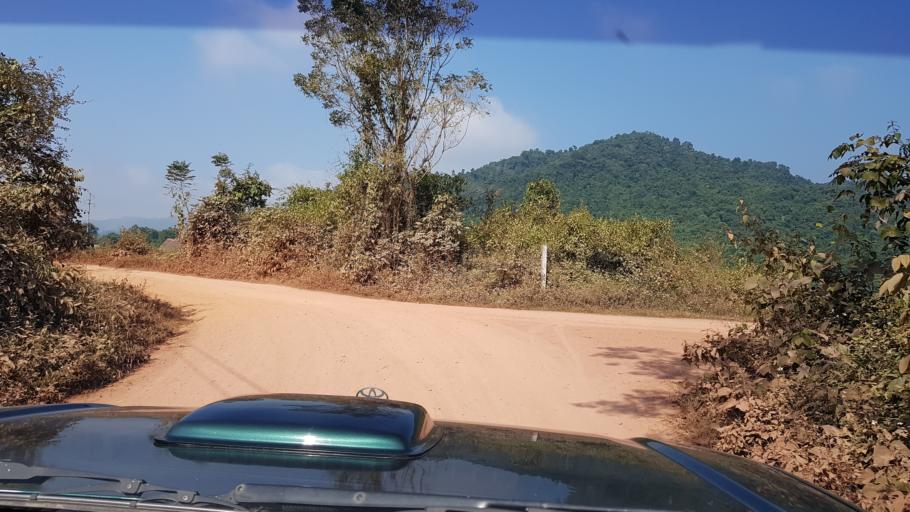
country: LA
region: Oudomxai
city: Muang Xay
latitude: 20.7162
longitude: 102.0404
